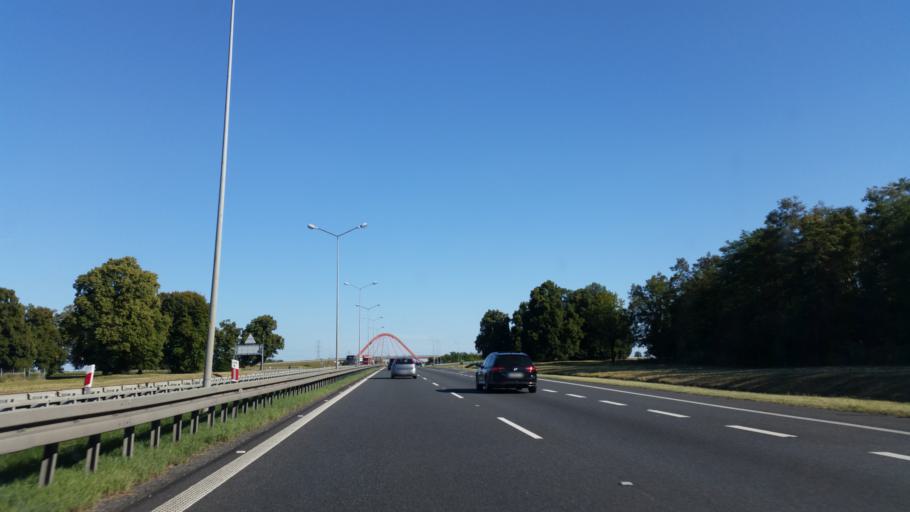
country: PL
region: Lower Silesian Voivodeship
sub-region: Powiat olawski
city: Wierzbno
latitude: 50.8817
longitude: 17.1987
